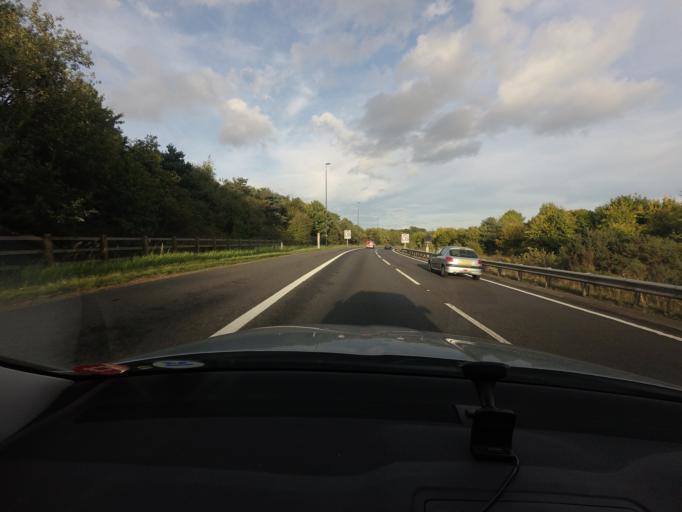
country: GB
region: England
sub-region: Kent
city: West Malling
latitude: 51.3087
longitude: 0.3584
